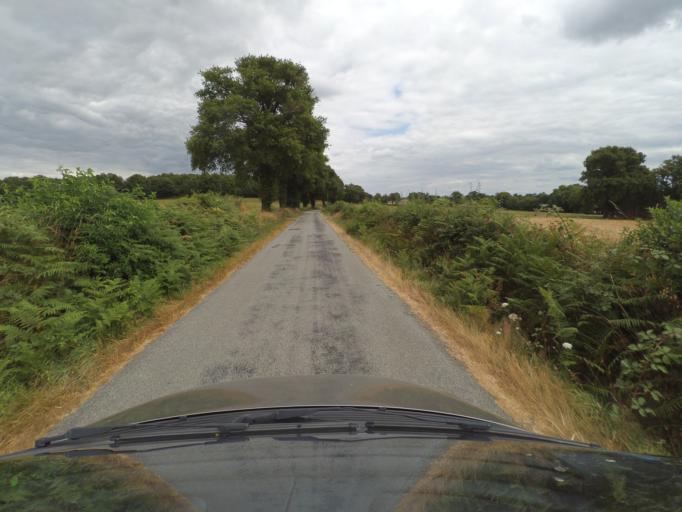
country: FR
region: Limousin
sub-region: Departement de la Haute-Vienne
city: Arnac-la-Poste
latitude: 46.2380
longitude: 1.3440
